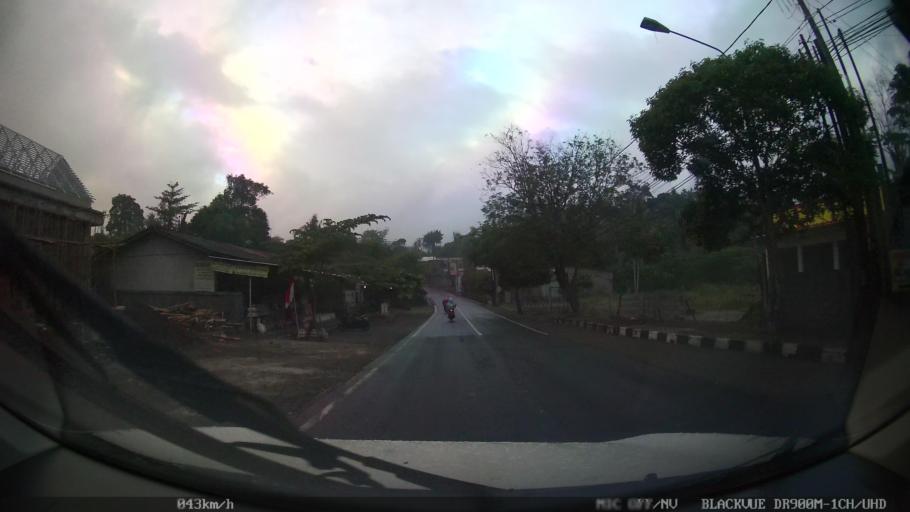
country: ID
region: Bali
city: Banjar Parekan
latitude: -8.5833
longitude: 115.2152
